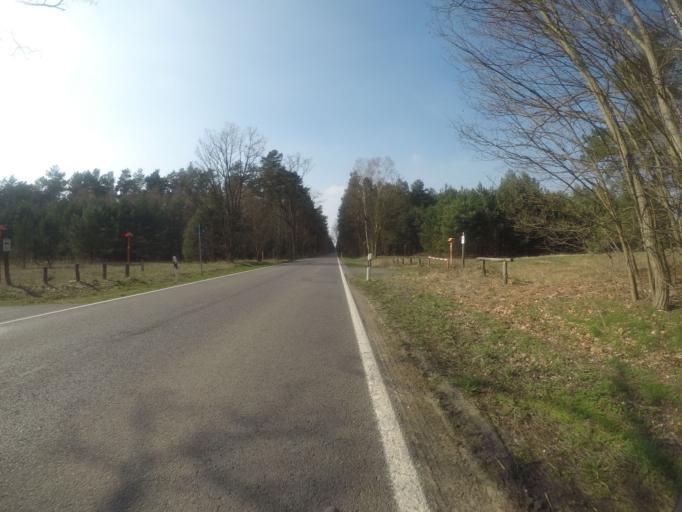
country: DE
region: Brandenburg
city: Bestensee
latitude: 52.2825
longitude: 13.7337
